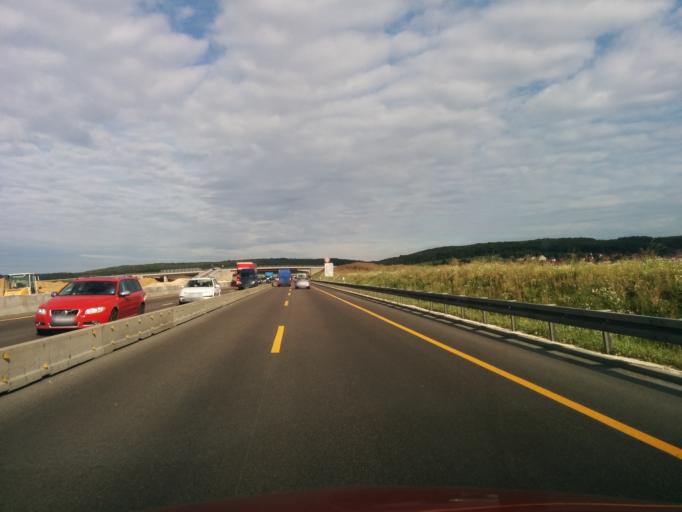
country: DE
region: Baden-Wuerttemberg
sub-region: Tuebingen Region
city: Dornstadt
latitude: 48.4817
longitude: 9.8699
